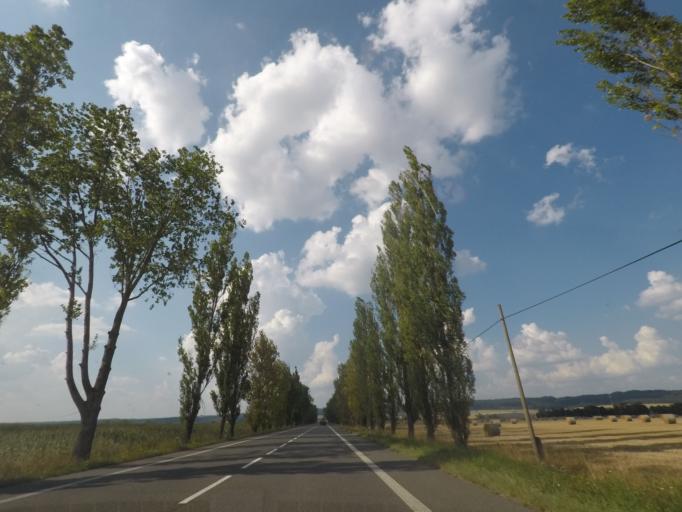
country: CZ
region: Kralovehradecky
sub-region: Okres Nachod
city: Jaromer
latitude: 50.4112
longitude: 15.8851
